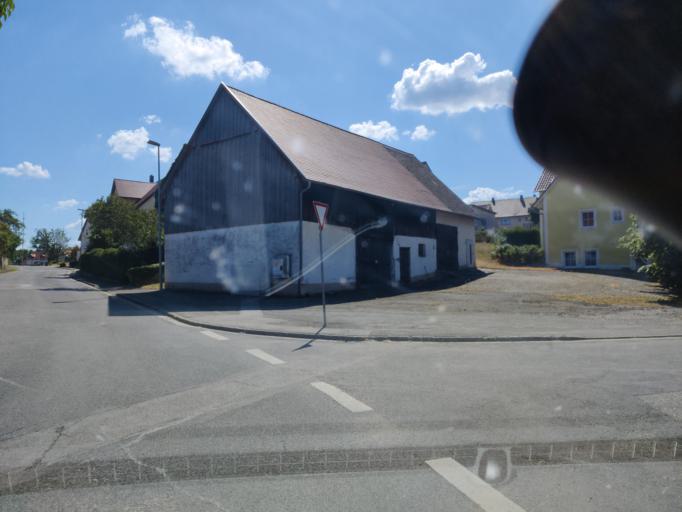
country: DE
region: Bavaria
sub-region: Regierungsbezirk Mittelfranken
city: Bergen
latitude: 49.0994
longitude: 11.1341
